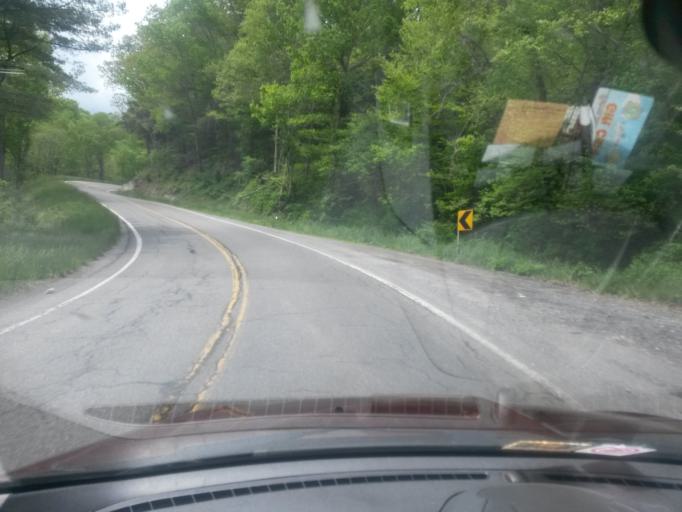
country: US
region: Virginia
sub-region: Floyd County
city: Floyd
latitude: 36.8910
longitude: -80.3230
